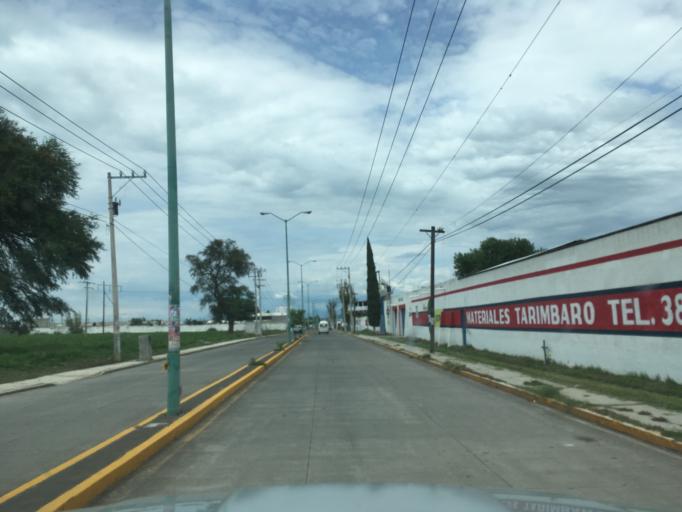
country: MX
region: Michoacan
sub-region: Tarimbaro
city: Meson Nuevo (Canada de la Magdalena)
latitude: 19.7965
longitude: -101.1686
